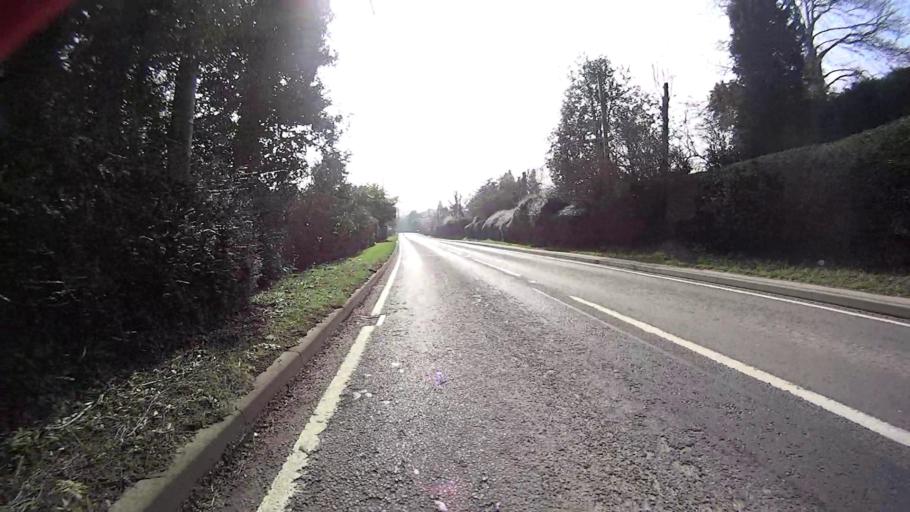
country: GB
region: England
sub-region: Surrey
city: Headley
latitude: 51.2528
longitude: -0.2662
